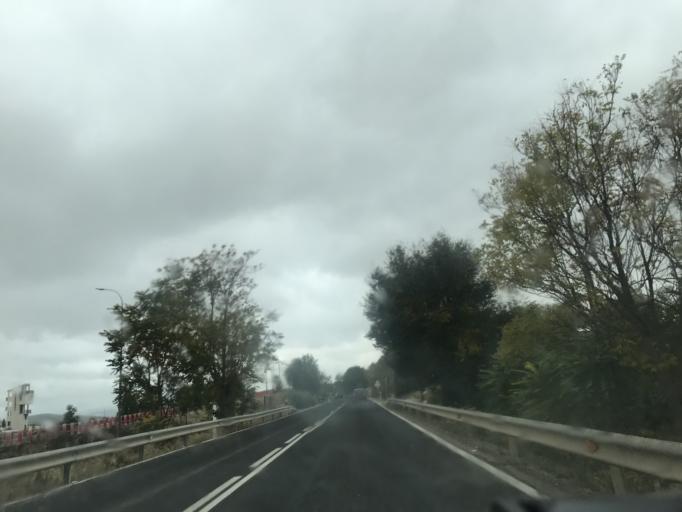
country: ES
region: Andalusia
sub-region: Provincia de Jaen
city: Peal de Becerro
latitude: 37.9164
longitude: -3.1070
